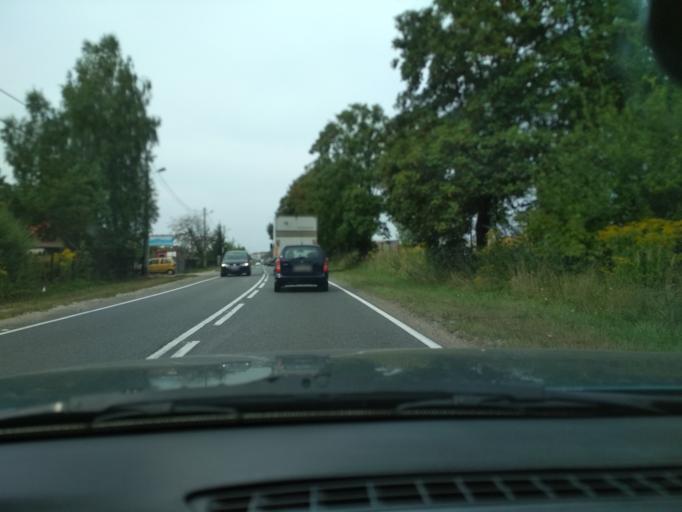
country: PL
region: Silesian Voivodeship
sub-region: Powiat zawiercianski
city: Zawiercie
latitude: 50.4699
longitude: 19.4039
